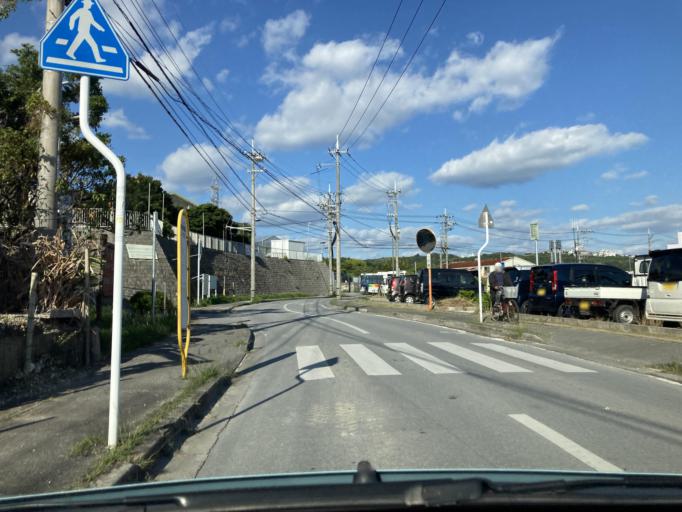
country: JP
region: Okinawa
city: Ginowan
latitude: 26.2218
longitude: 127.7588
